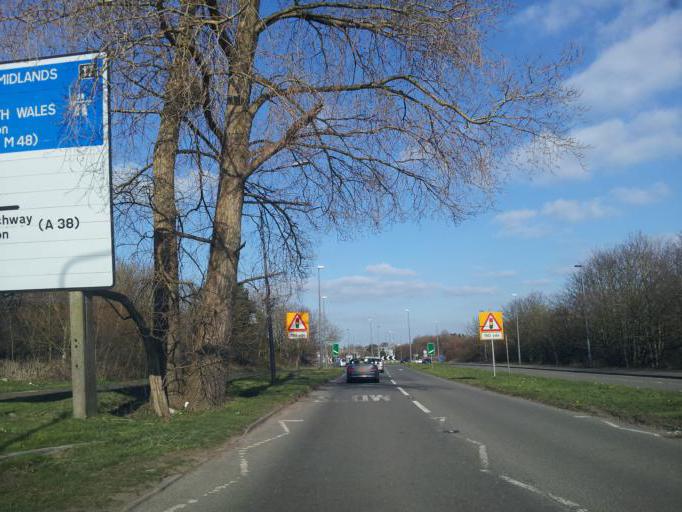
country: GB
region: England
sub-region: South Gloucestershire
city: Almondsbury
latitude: 51.5269
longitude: -2.6122
